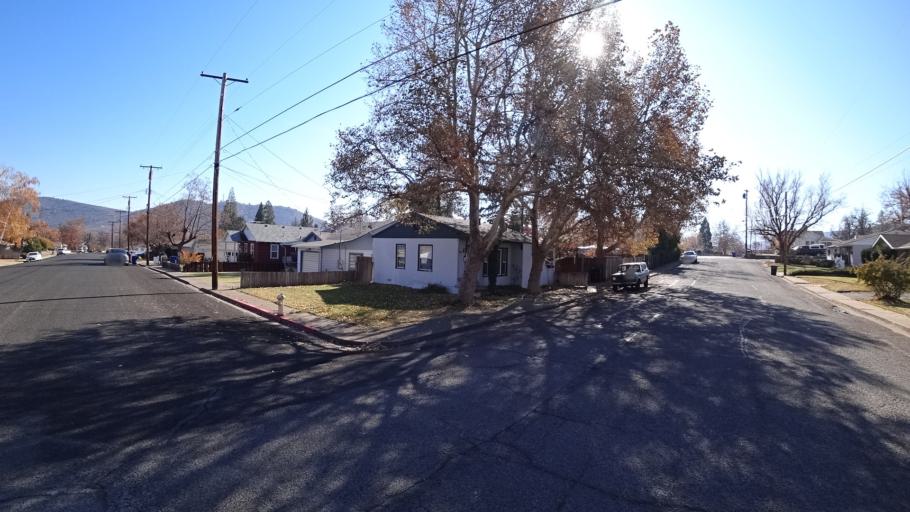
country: US
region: California
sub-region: Siskiyou County
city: Yreka
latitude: 41.7300
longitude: -122.6465
